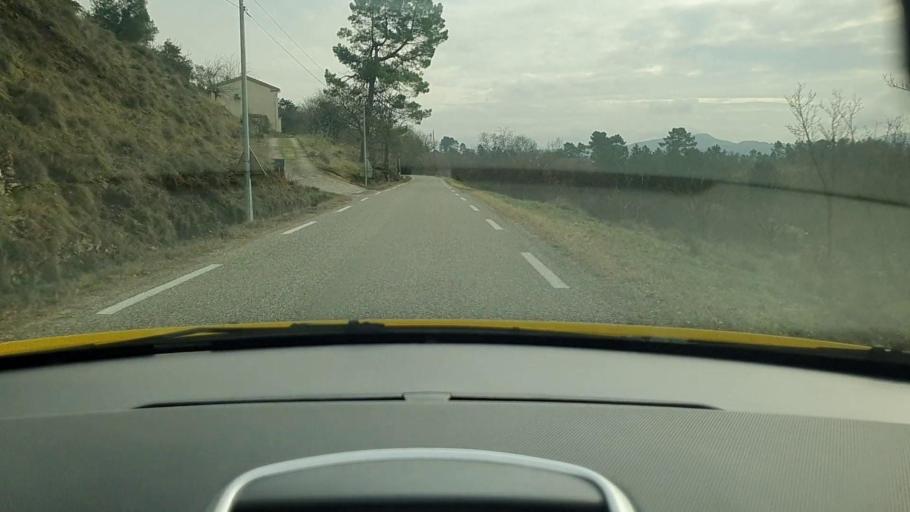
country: FR
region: Languedoc-Roussillon
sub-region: Departement du Gard
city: Besseges
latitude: 44.3178
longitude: 4.0702
